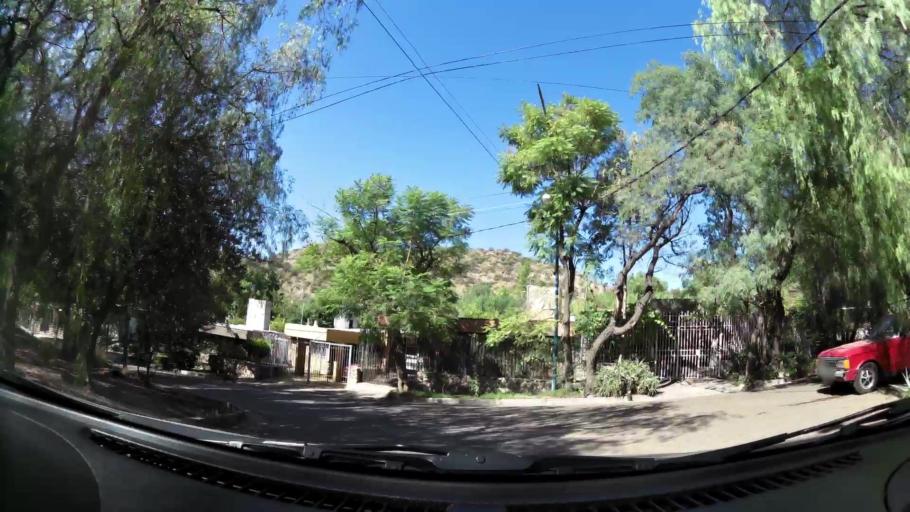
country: AR
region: Mendoza
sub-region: Departamento de Godoy Cruz
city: Godoy Cruz
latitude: -32.9025
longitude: -68.8933
